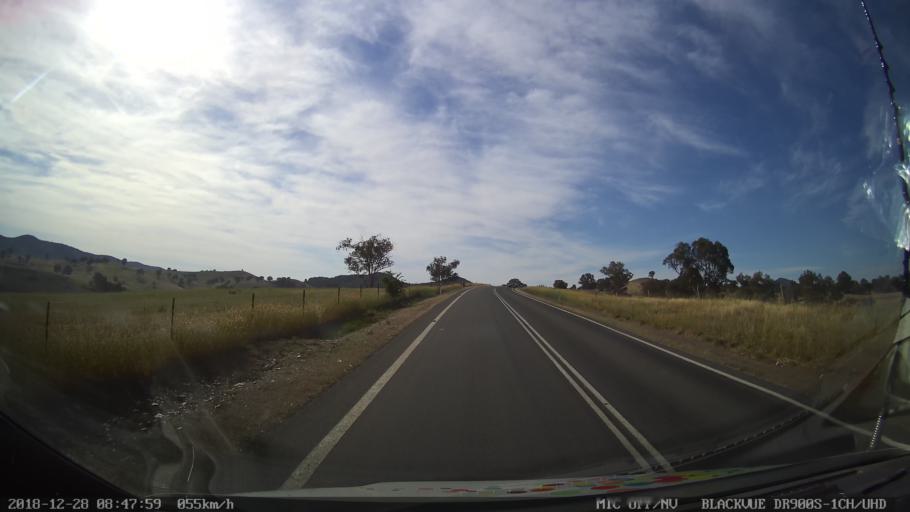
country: AU
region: New South Wales
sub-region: Upper Lachlan Shire
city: Crookwell
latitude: -34.0315
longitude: 149.3361
